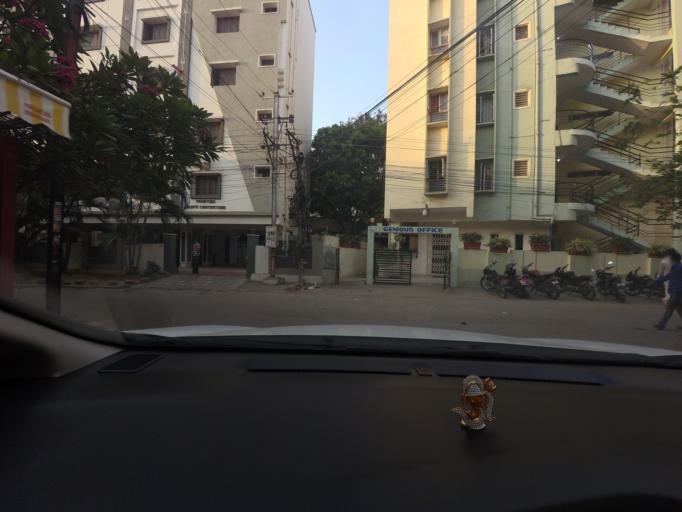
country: IN
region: Telangana
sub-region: Rangareddi
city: Kukatpalli
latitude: 17.4448
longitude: 78.3879
